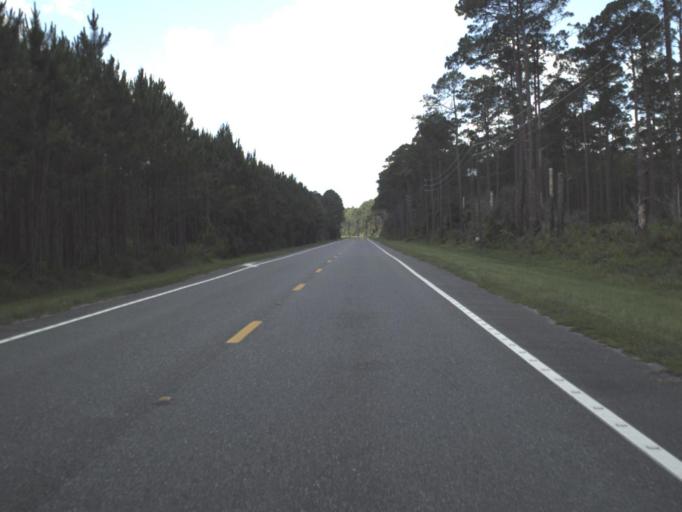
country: US
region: Florida
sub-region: Levy County
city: Williston Highlands
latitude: 29.2078
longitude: -82.5887
